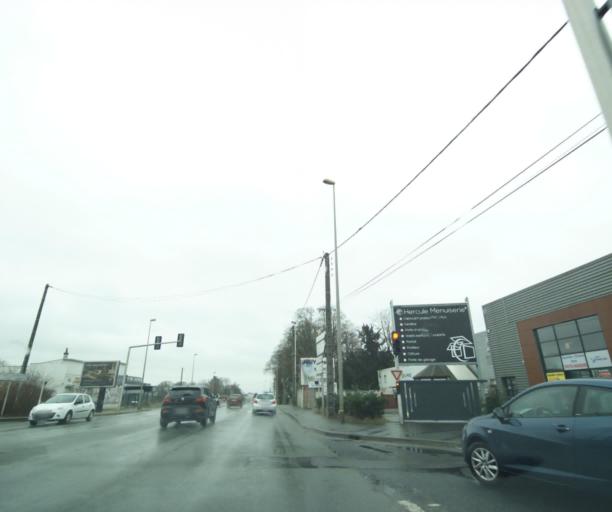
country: FR
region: Centre
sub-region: Departement du Loiret
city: Saran
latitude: 47.9434
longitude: 1.8925
